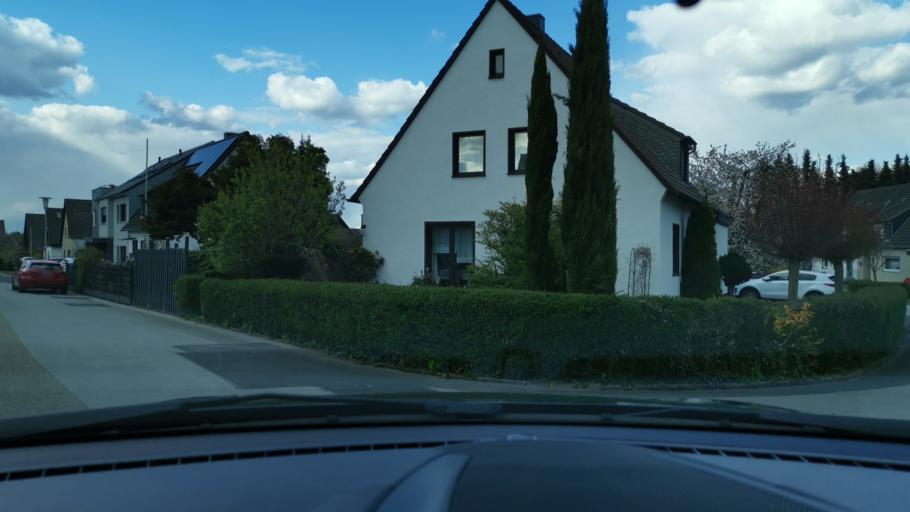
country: DE
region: North Rhine-Westphalia
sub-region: Regierungsbezirk Dusseldorf
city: Grevenbroich
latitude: 51.0697
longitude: 6.5961
